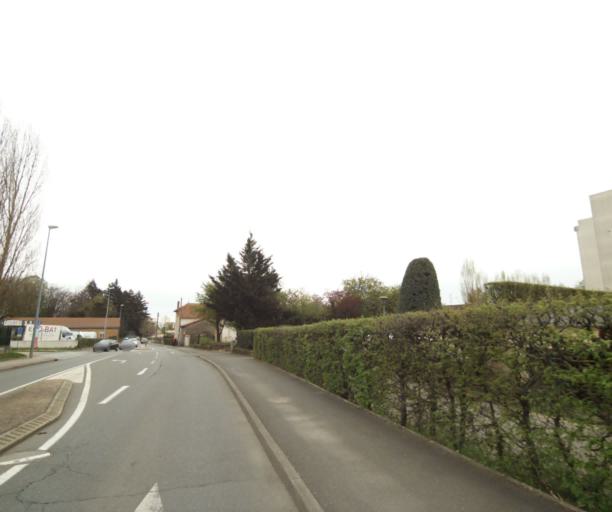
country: FR
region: Bourgogne
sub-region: Departement de Saone-et-Loire
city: Macon
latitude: 46.3111
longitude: 4.8110
